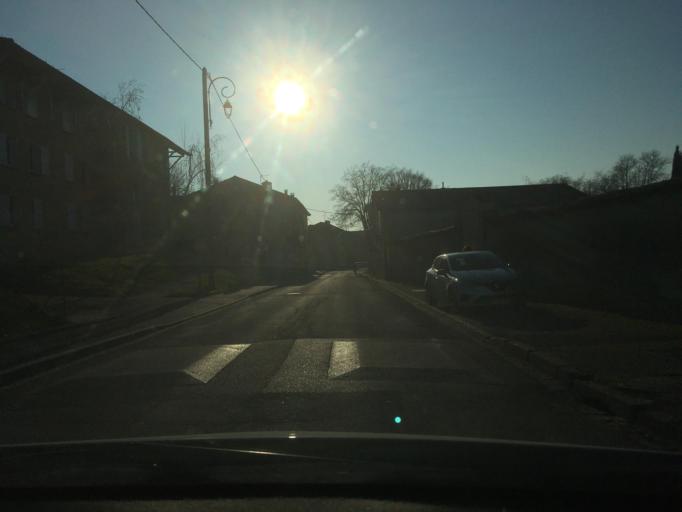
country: FR
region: Rhone-Alpes
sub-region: Departement de l'Ain
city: Ars-sur-Formans
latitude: 45.9943
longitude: 4.8196
